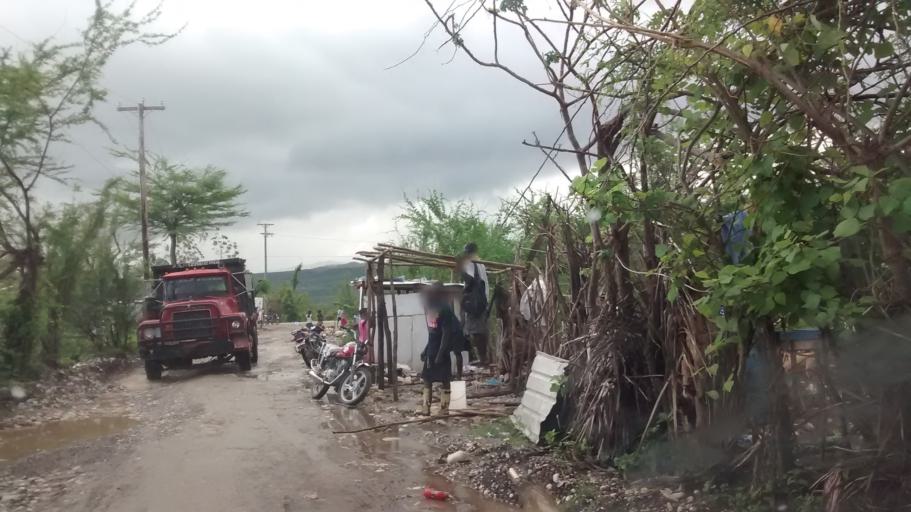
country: HT
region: Grandans
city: Jeremie
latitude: 18.6206
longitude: -74.0920
